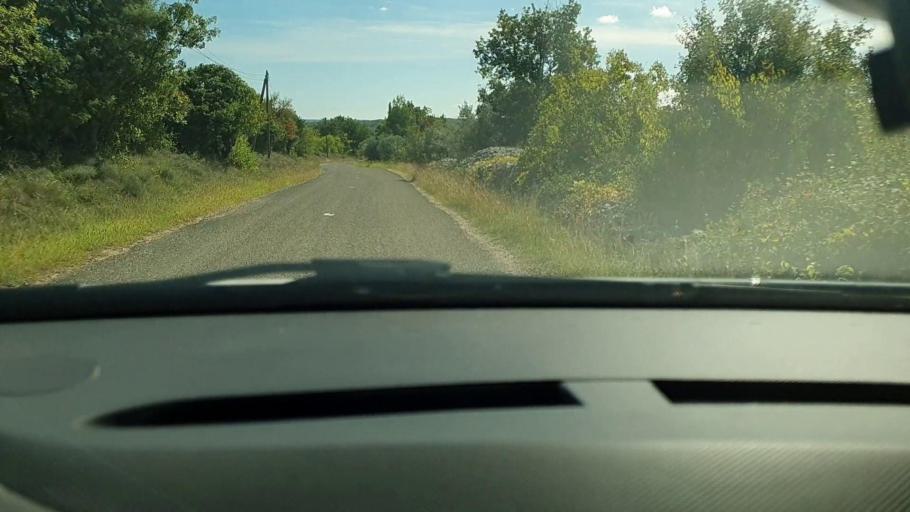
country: FR
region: Languedoc-Roussillon
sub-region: Departement du Gard
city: Barjac
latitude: 44.1899
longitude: 4.3229
